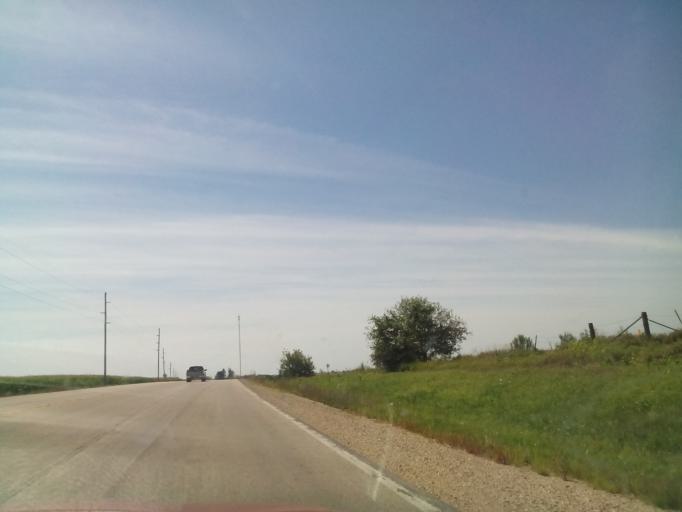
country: US
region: Wisconsin
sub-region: Green County
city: Monticello
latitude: 42.6757
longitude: -89.6169
